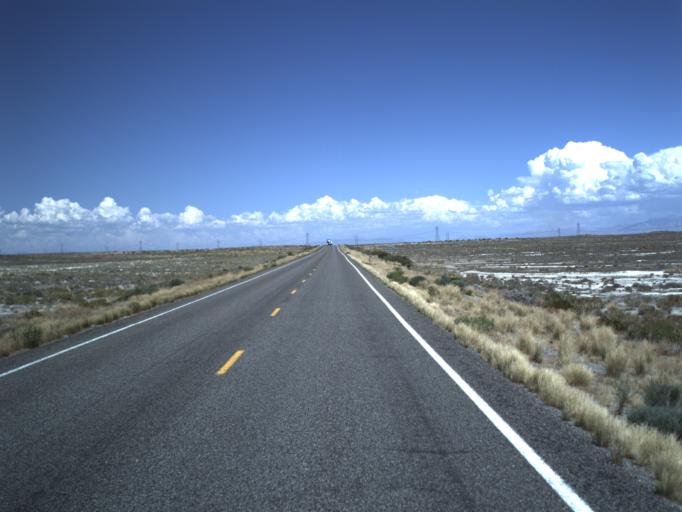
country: US
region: Utah
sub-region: Millard County
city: Delta
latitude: 39.2313
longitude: -112.9302
